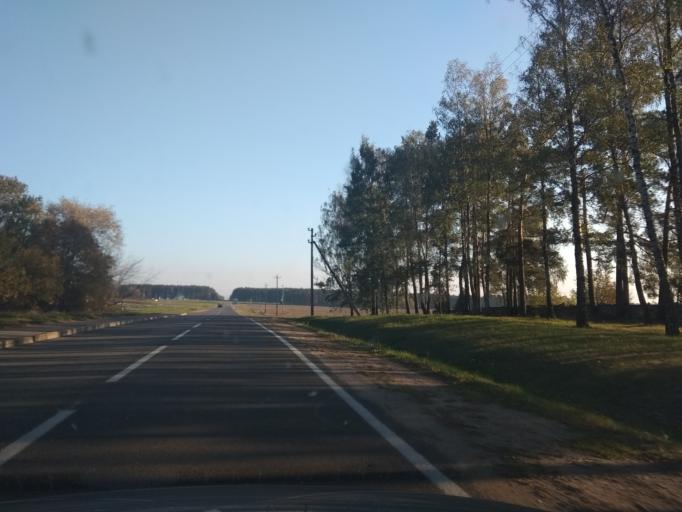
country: BY
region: Grodnenskaya
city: Vawkavysk
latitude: 53.1526
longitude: 24.4978
